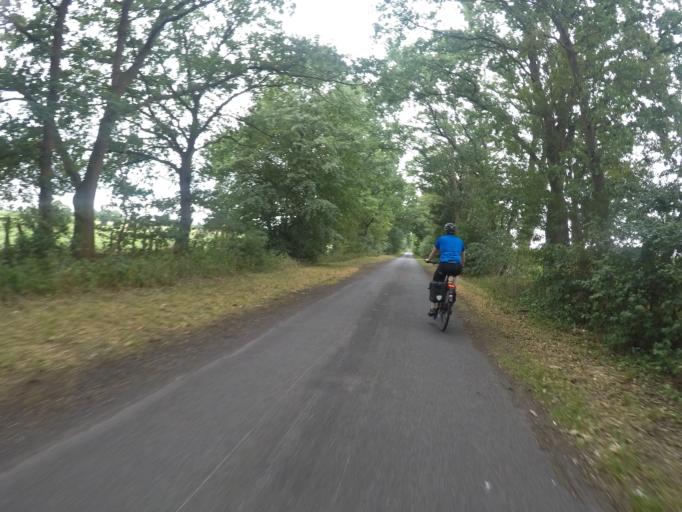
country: DE
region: Lower Saxony
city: Wingst
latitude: 53.6956
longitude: 9.0907
